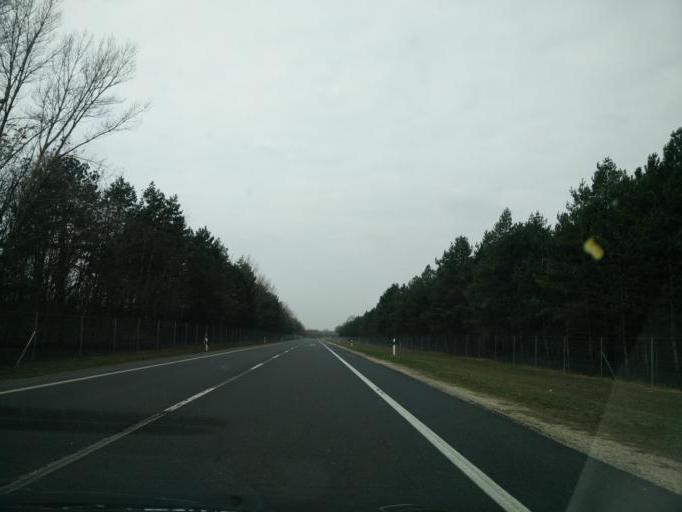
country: HU
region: Gyor-Moson-Sopron
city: Gyor
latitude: 47.7162
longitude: 17.7027
